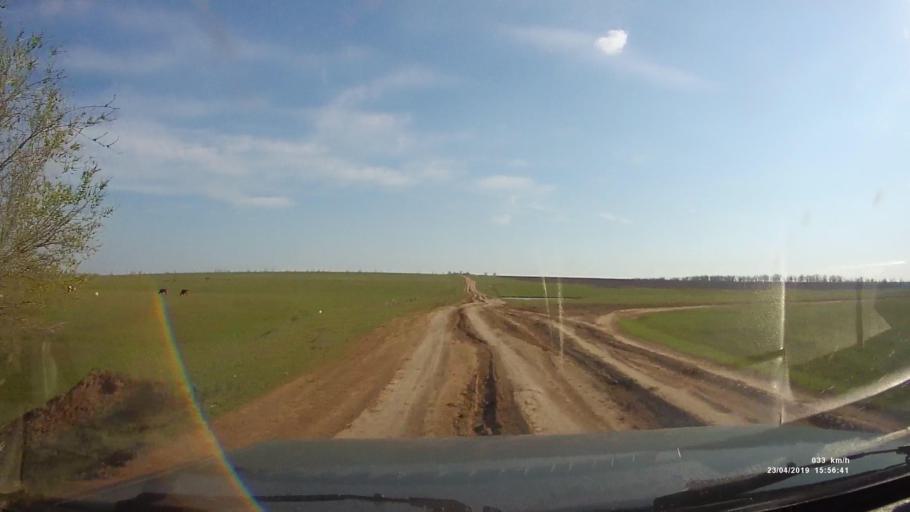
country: RU
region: Rostov
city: Remontnoye
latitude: 46.5357
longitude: 43.1109
